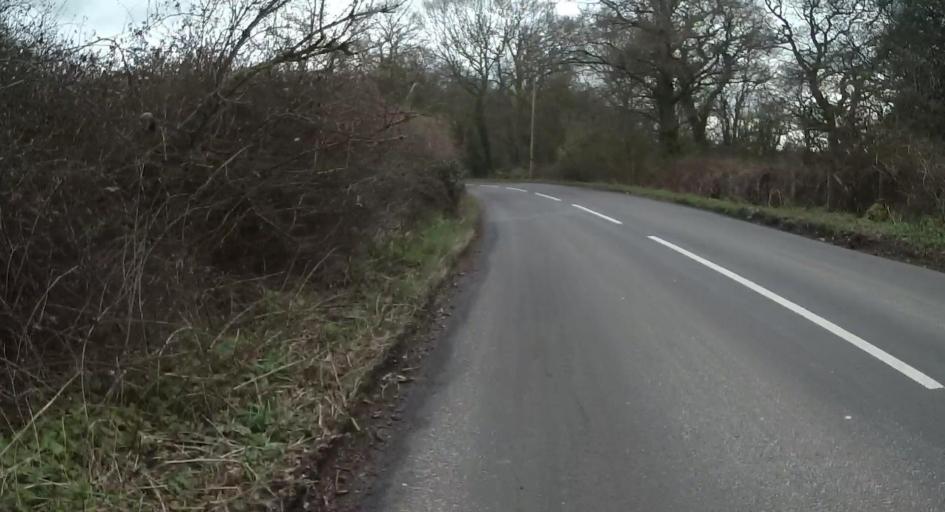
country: GB
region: England
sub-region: Hampshire
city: Alton
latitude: 51.1781
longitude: -0.9834
